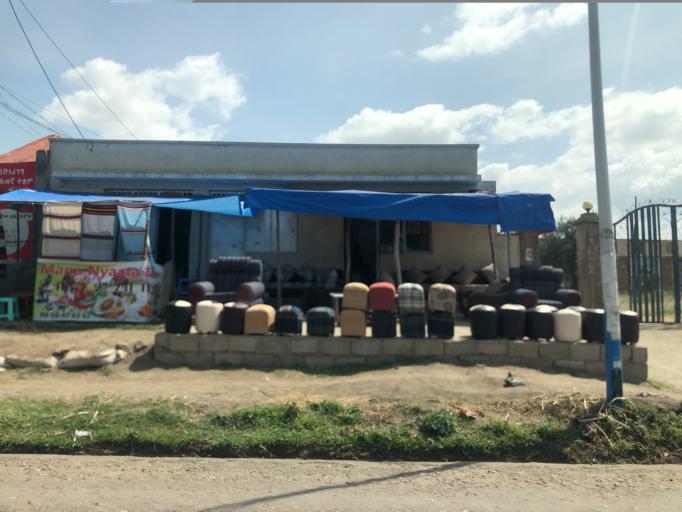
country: ET
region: Oromiya
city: Shashemene
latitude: 7.2017
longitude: 38.6073
